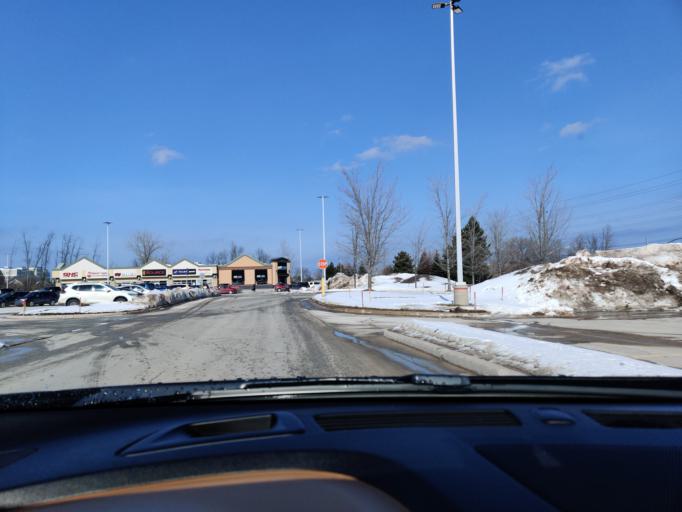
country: CA
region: Ontario
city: Collingwood
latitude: 44.5043
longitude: -80.2360
